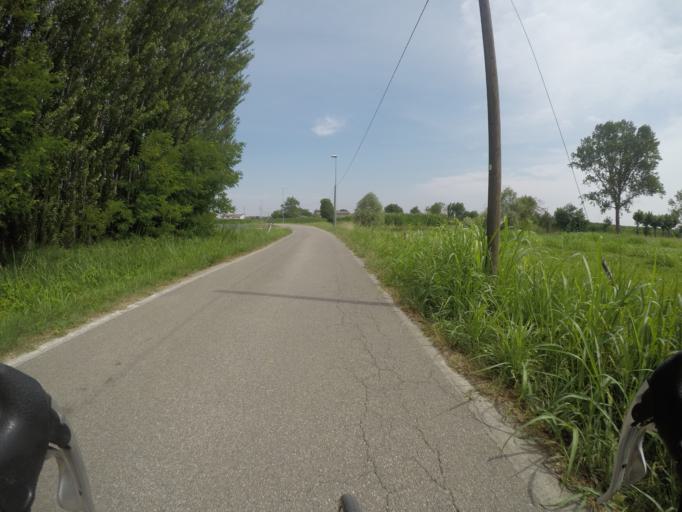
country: IT
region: Veneto
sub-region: Provincia di Rovigo
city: Villanova del Ghebbo Canton
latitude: 45.0468
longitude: 11.6575
